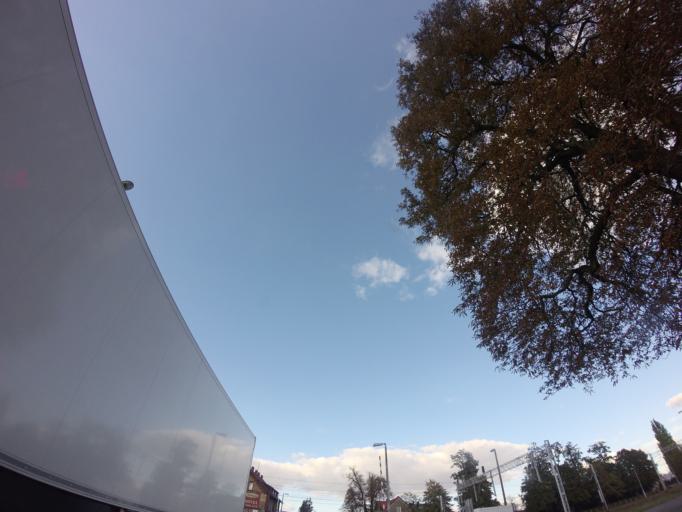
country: PL
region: Greater Poland Voivodeship
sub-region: Powiat nowotomyski
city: Nowy Tomysl
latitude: 52.3038
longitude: 16.1281
